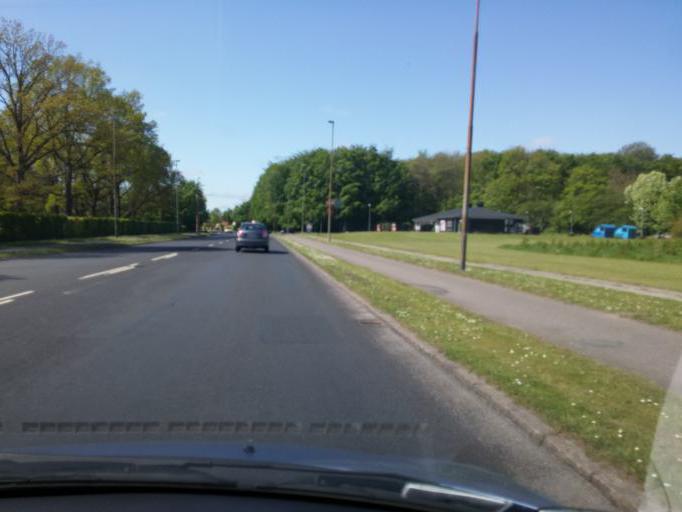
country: DK
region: South Denmark
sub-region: Odense Kommune
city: Stige
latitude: 55.4157
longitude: 10.4177
